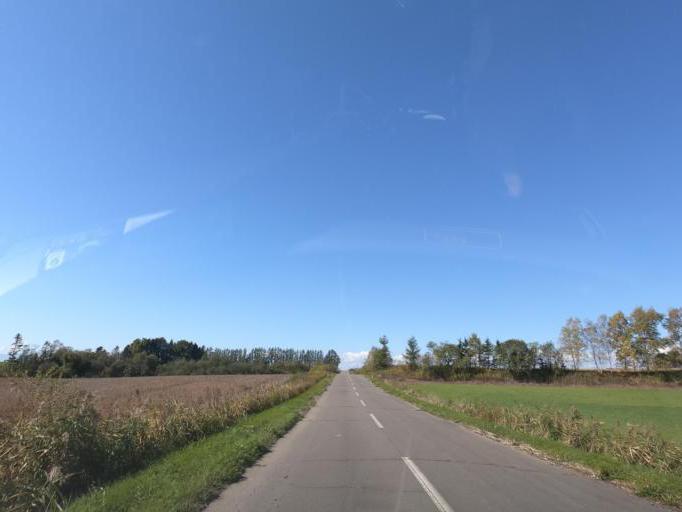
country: JP
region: Hokkaido
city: Otofuke
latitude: 43.0596
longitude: 143.2750
